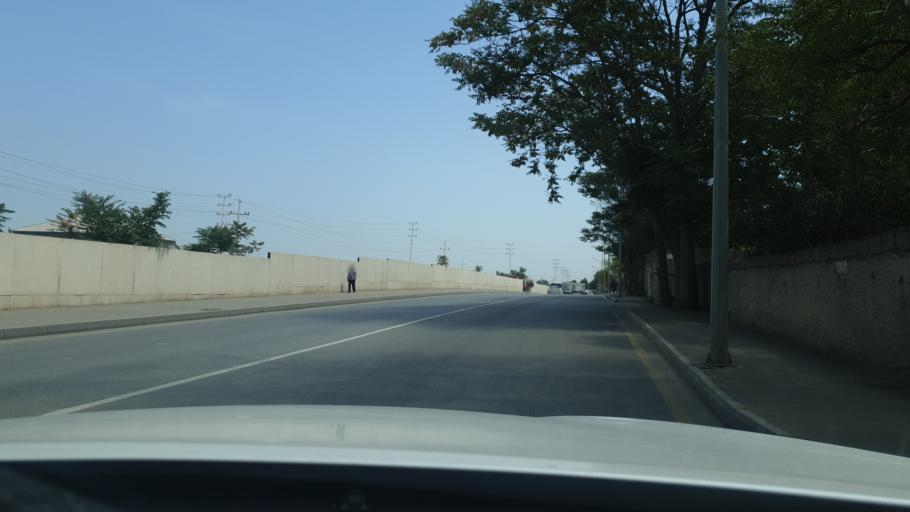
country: AZ
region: Baki
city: Qaracuxur
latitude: 40.3930
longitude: 49.9768
